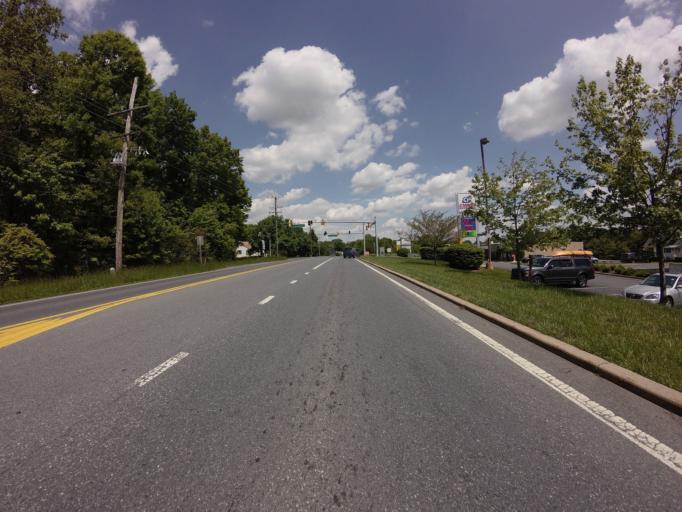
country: US
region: Maryland
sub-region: Frederick County
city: Green Valley
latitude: 39.3436
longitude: -77.2588
